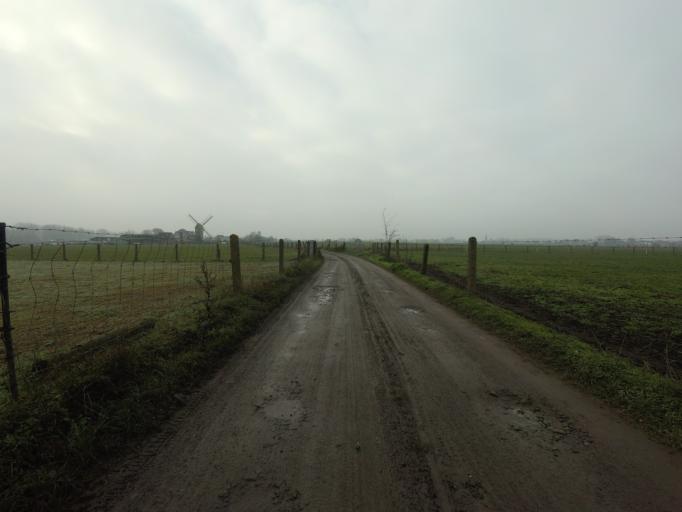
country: BE
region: Flanders
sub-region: Provincie Oost-Vlaanderen
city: Ninove
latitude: 50.8203
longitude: 3.9814
